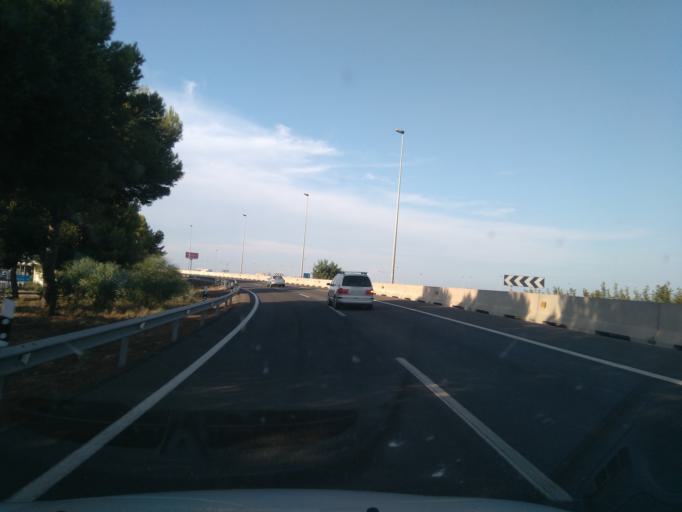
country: ES
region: Valencia
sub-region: Provincia de Valencia
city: Silla
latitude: 39.3430
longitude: -0.4278
